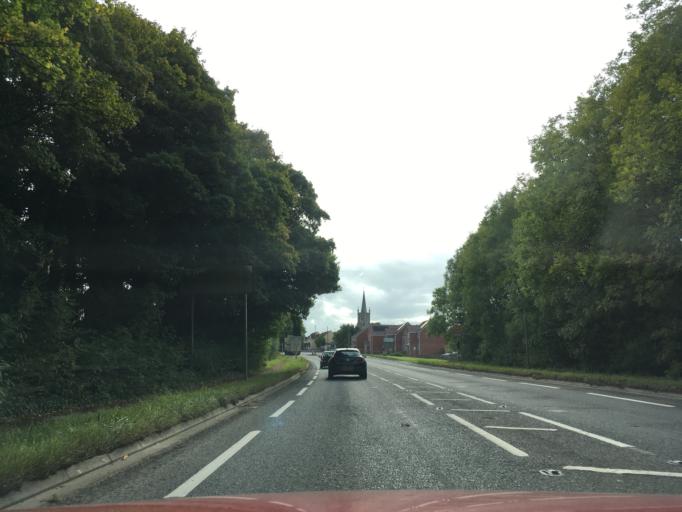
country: GB
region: England
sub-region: South Gloucestershire
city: Falfield
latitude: 51.6587
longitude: -2.4547
